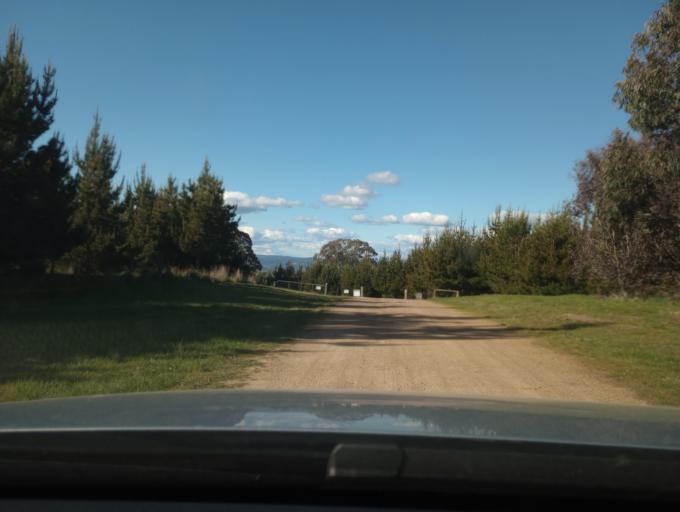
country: AU
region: New South Wales
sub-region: Blayney
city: Millthorpe
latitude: -33.4080
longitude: 149.3148
